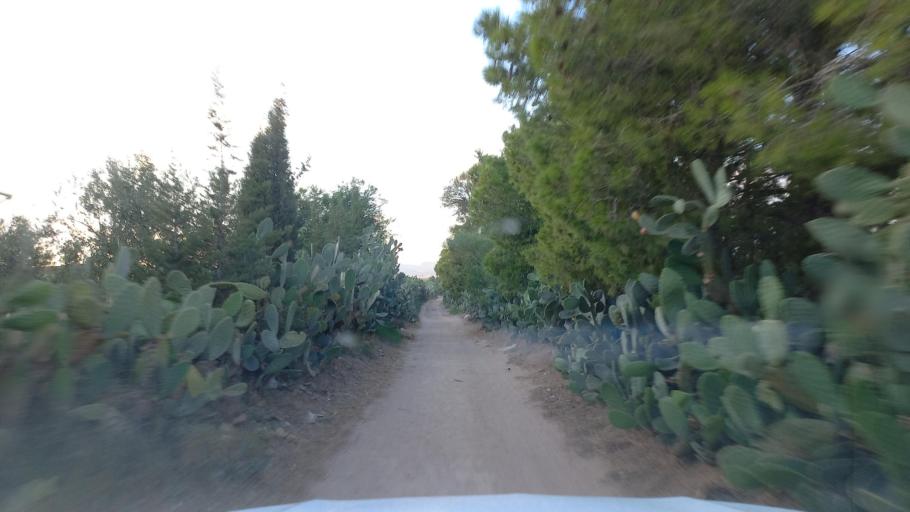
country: TN
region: Al Qasrayn
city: Sbiba
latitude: 35.3779
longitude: 9.0553
